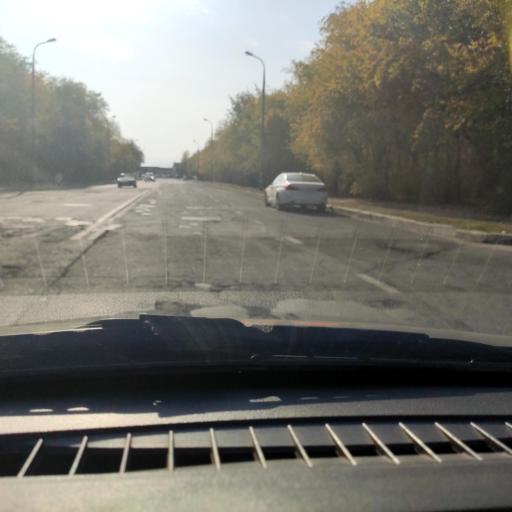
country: RU
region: Samara
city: Tol'yatti
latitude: 53.5040
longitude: 49.2525
